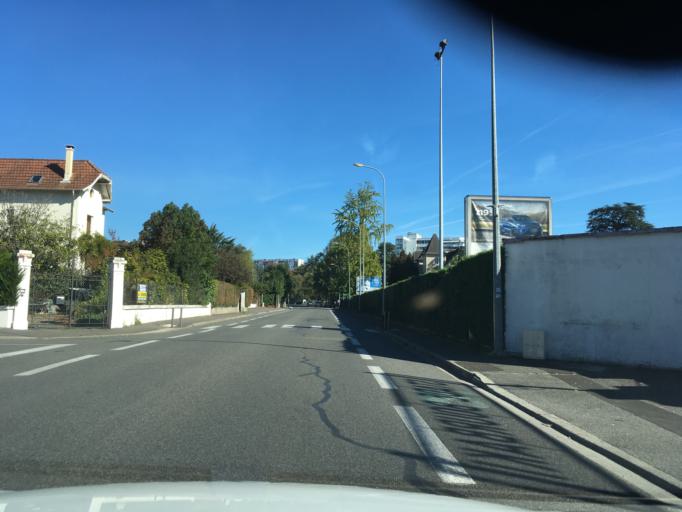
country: FR
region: Aquitaine
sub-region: Departement des Pyrenees-Atlantiques
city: Pau
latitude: 43.3084
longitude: -0.3745
